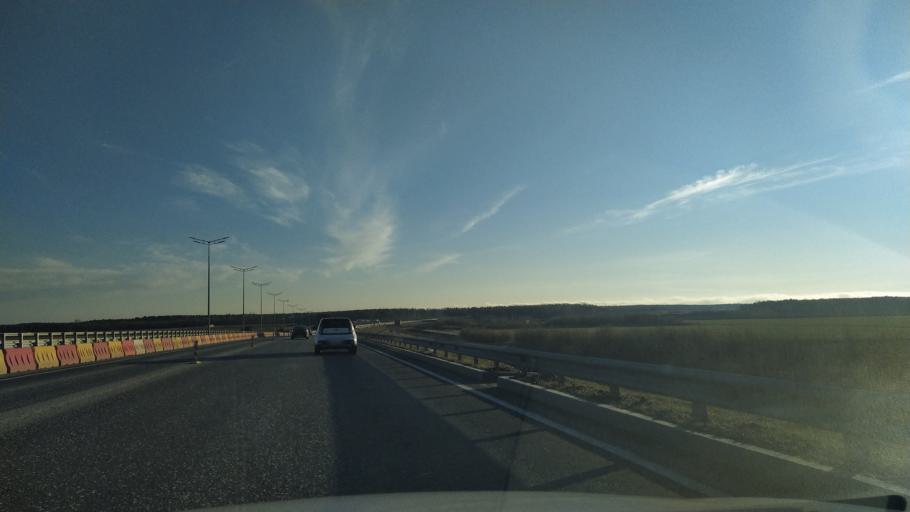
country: RU
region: St.-Petersburg
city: Pargolovo
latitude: 60.0908
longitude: 30.2422
